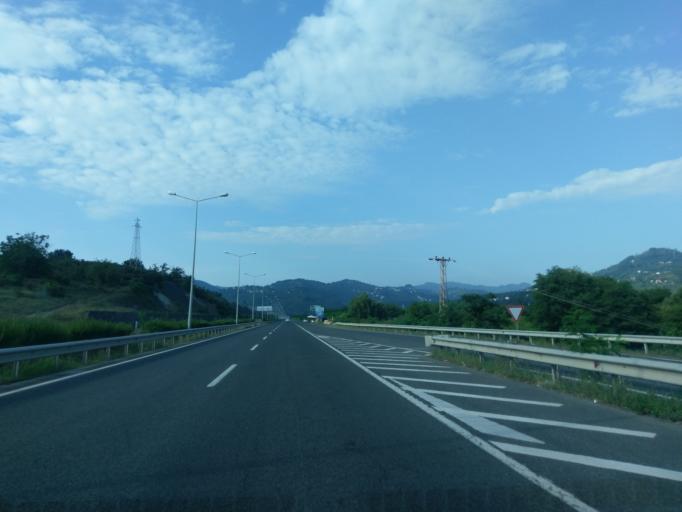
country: TR
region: Ordu
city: Ordu
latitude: 41.0057
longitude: 37.8269
